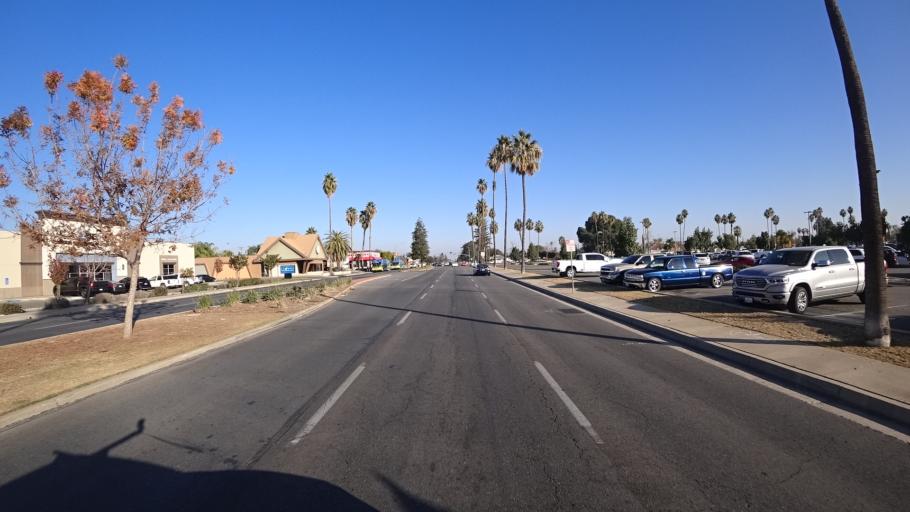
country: US
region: California
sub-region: Kern County
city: Bakersfield
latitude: 35.3394
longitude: -119.0319
